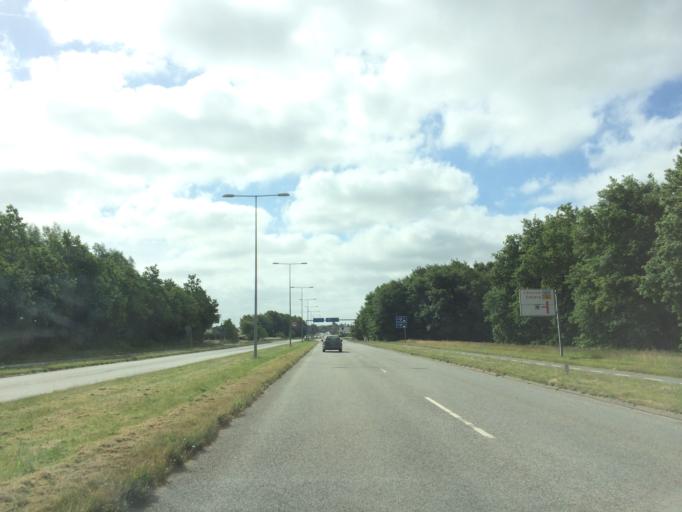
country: DK
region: Central Jutland
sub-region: Herning Kommune
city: Herning
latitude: 56.1446
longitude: 8.9400
